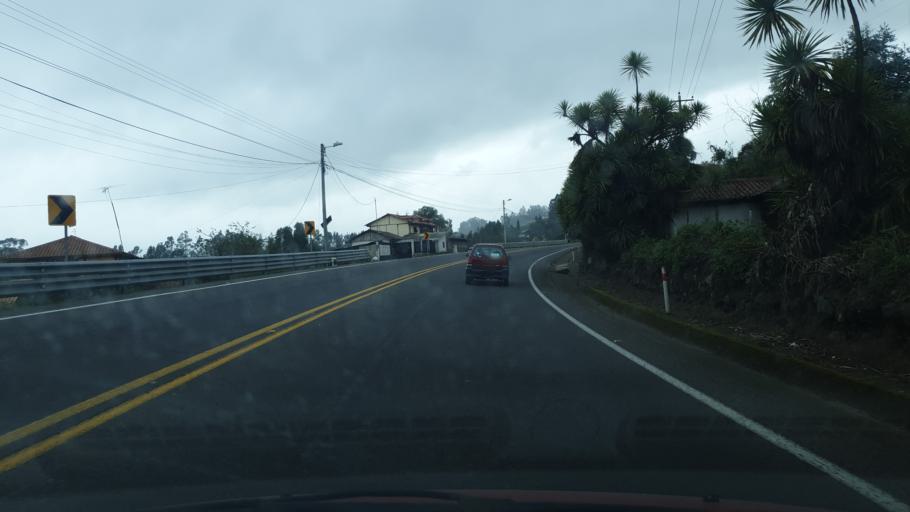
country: EC
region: Tungurahua
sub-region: Canton Quero
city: Quero
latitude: -1.3852
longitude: -78.6463
